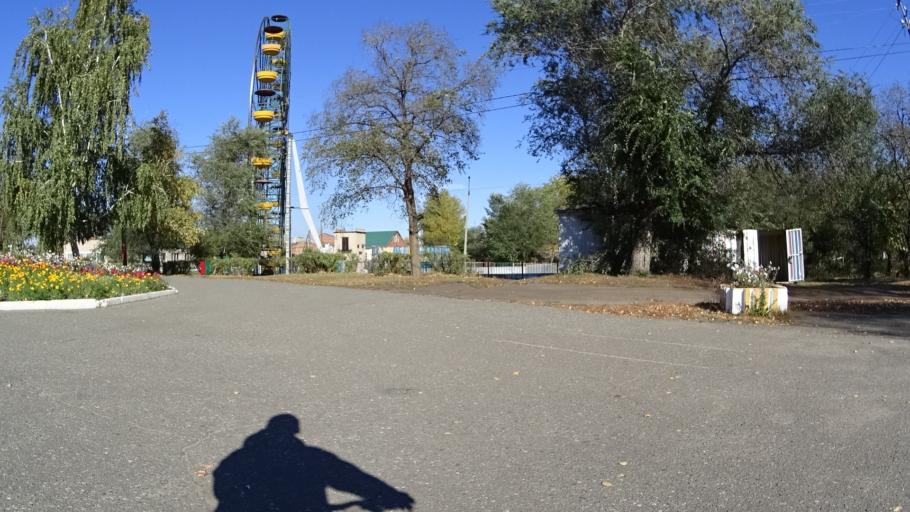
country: RU
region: Chelyabinsk
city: Troitsk
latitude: 54.0845
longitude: 61.5521
